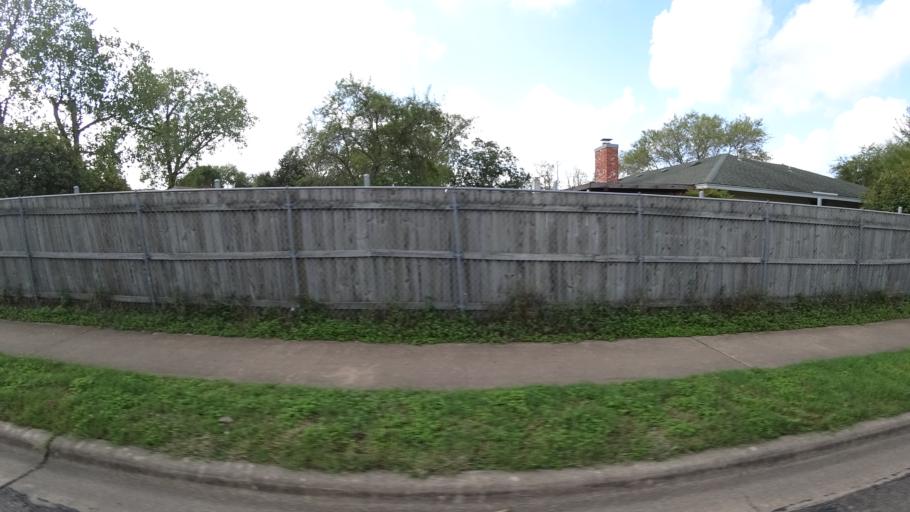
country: US
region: Texas
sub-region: Travis County
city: Rollingwood
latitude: 30.2185
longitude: -97.8048
